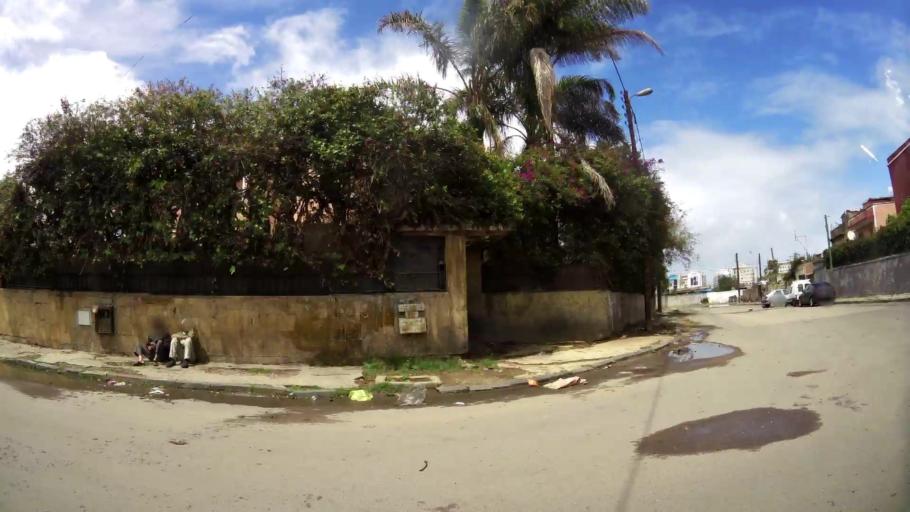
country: MA
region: Grand Casablanca
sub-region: Casablanca
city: Casablanca
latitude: 33.5679
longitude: -7.6297
